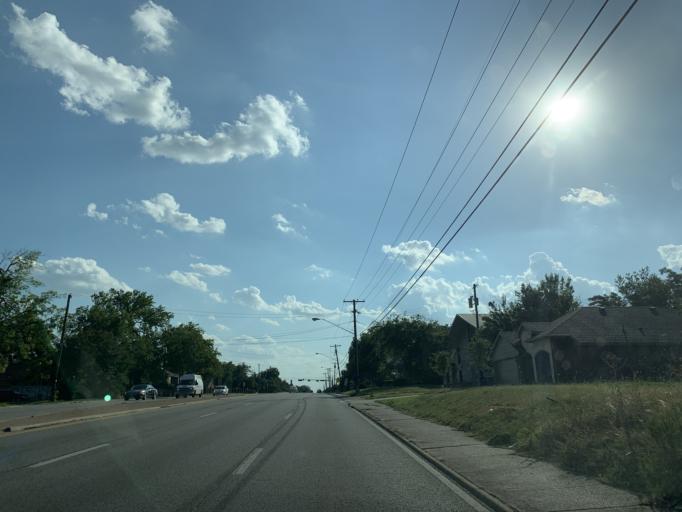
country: US
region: Texas
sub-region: Dallas County
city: Hutchins
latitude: 32.6918
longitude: -96.7779
